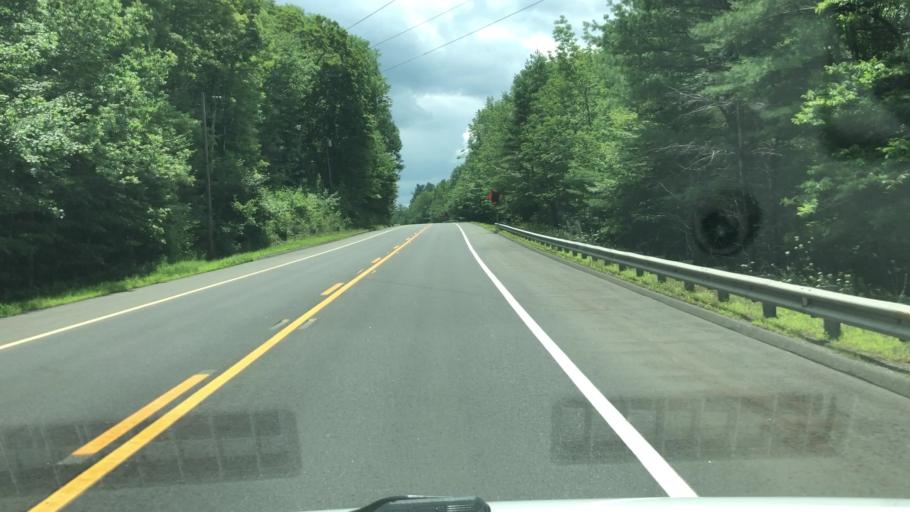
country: US
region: Massachusetts
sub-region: Franklin County
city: Ashfield
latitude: 42.4782
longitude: -72.8102
